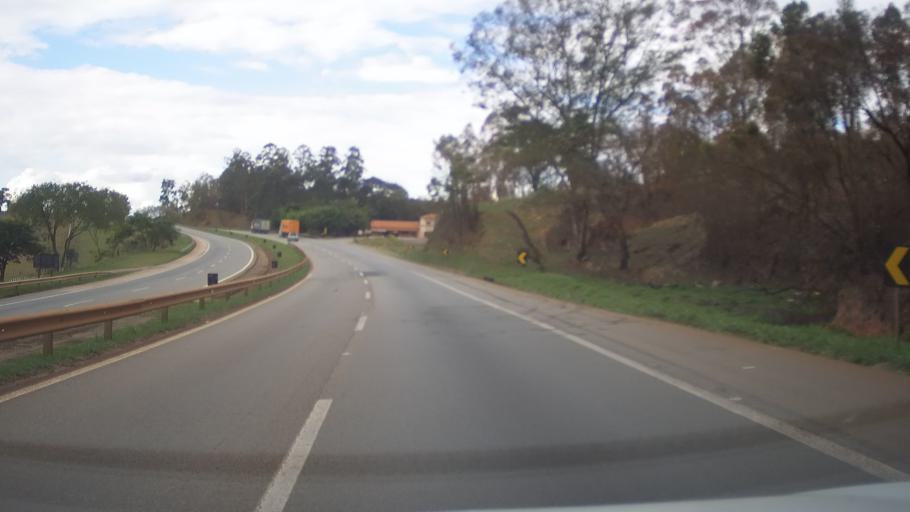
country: BR
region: Minas Gerais
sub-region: Itauna
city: Itauna
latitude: -20.2958
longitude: -44.4379
